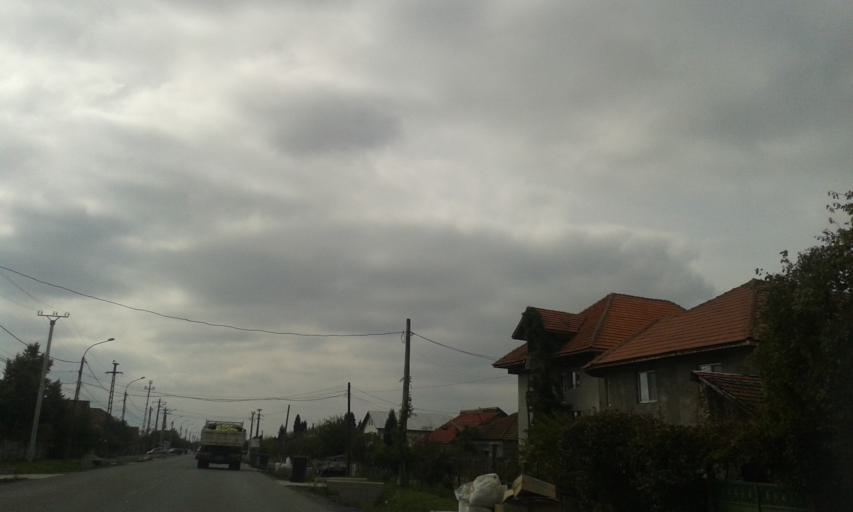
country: RO
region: Gorj
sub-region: Comuna Turcinesti
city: Turcinesti
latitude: 45.0999
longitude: 23.3346
